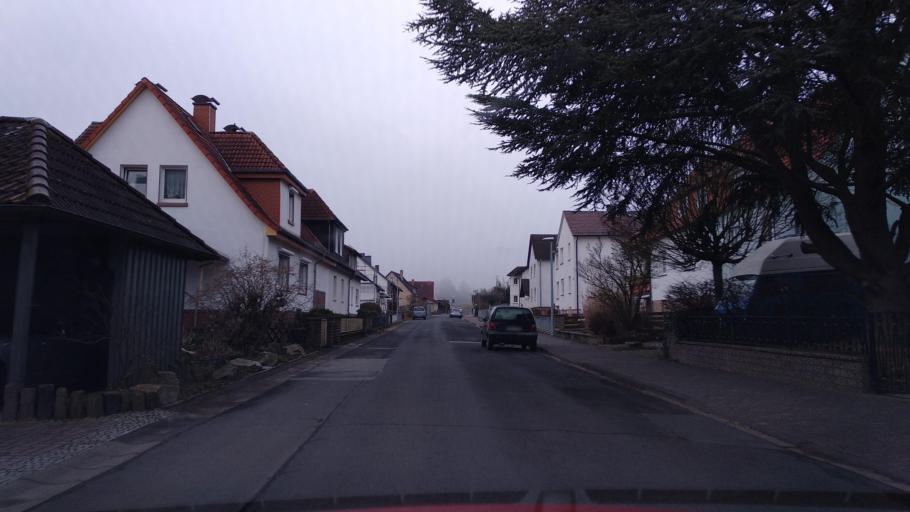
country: DE
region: Hesse
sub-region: Regierungsbezirk Kassel
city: Calden
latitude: 51.3656
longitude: 9.3872
